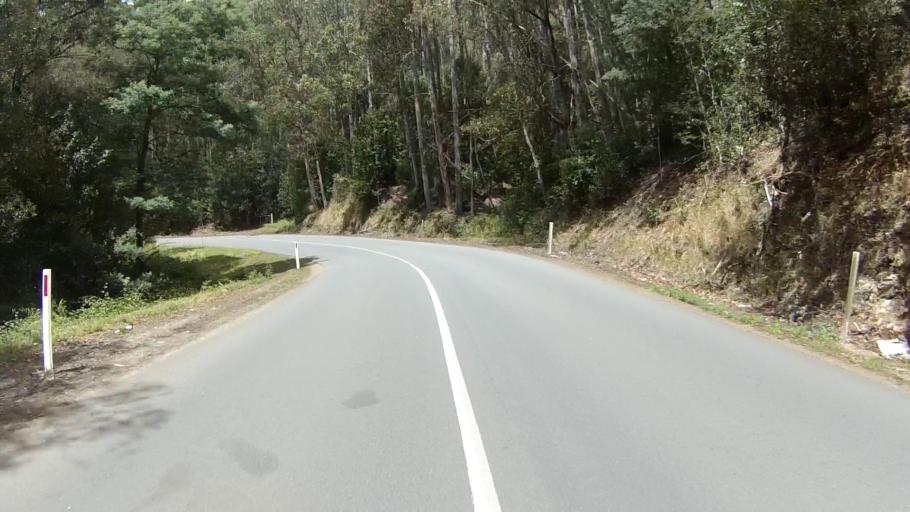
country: AU
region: Tasmania
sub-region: Kingborough
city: Kettering
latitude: -43.1283
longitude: 147.1670
